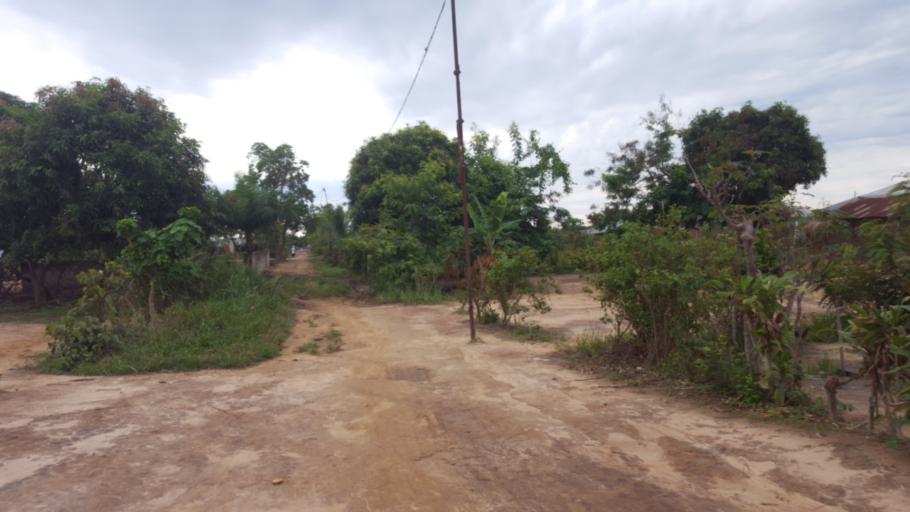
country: CD
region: Bandundu
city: Bandundu
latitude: -3.2998
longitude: 17.3807
